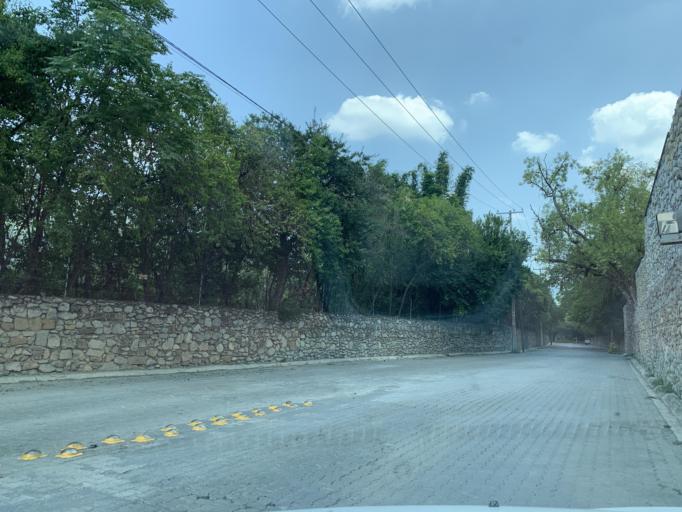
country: MX
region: Nuevo Leon
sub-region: Juarez
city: Bosques de San Pedro
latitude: 25.5170
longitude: -100.1997
